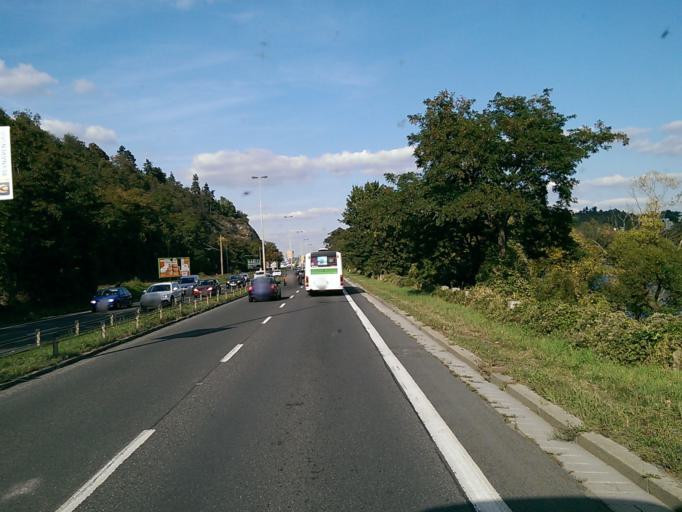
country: CZ
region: Praha
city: Branik
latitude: 50.0307
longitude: 14.3992
